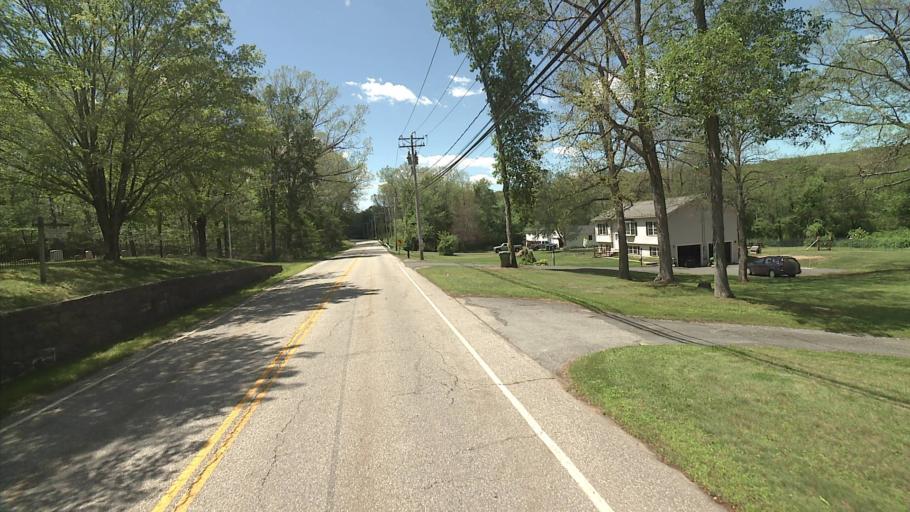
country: US
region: Connecticut
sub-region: Middlesex County
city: East Hampton
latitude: 41.5601
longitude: -72.5095
